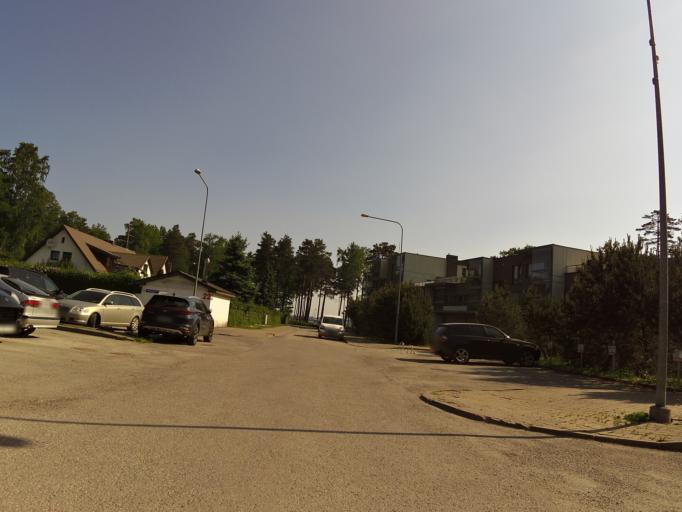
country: EE
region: Harju
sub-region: Saue vald
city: Laagri
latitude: 59.4405
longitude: 24.6233
